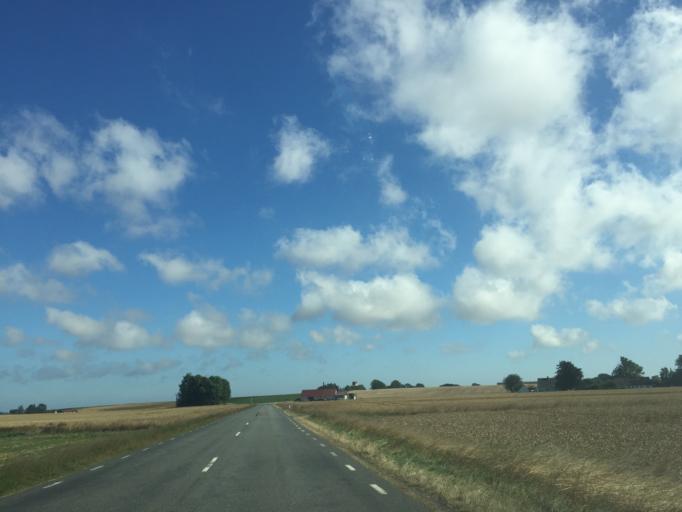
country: SE
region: Skane
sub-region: Ystads Kommun
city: Kopingebro
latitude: 55.4522
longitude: 14.1161
